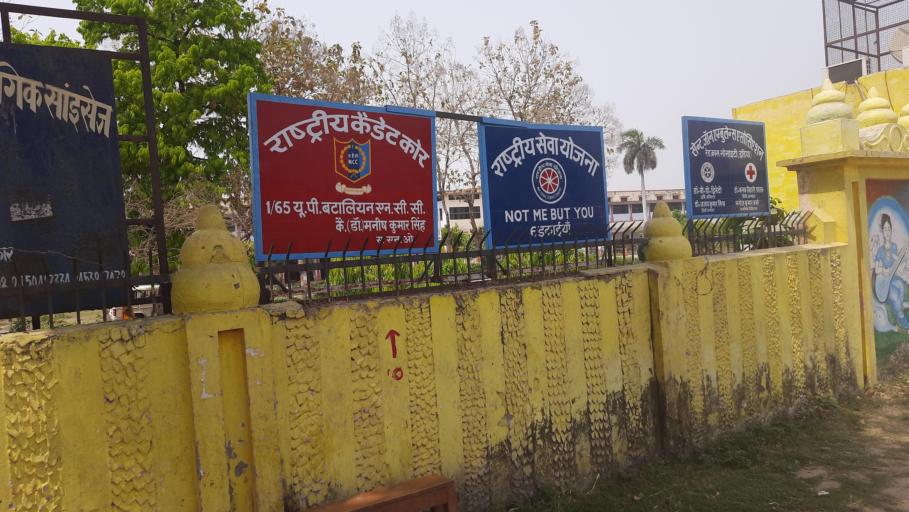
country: IN
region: Uttar Pradesh
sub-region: Faizabad
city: Ayodhya
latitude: 26.7845
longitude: 82.1873
